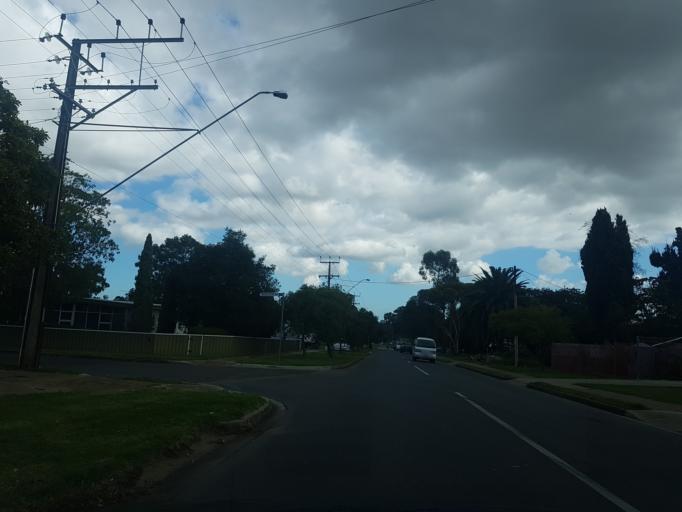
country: AU
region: South Australia
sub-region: Salisbury
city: Ingle Farm
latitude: -34.8120
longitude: 138.6492
